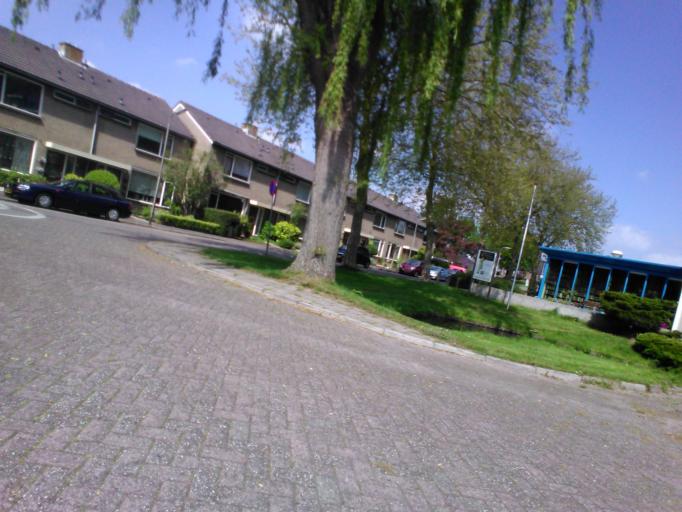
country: NL
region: South Holland
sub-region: Gemeente Rijnwoude
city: Benthuizen
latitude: 52.0957
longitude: 4.5826
